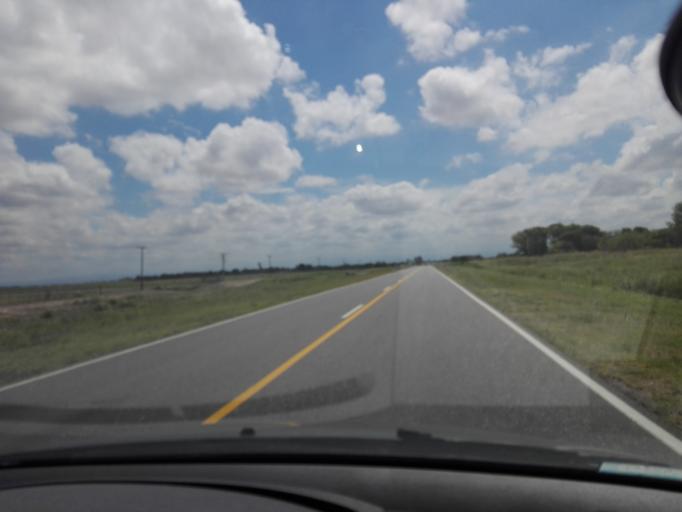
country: AR
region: Cordoba
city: Toledo
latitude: -31.6467
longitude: -64.0586
